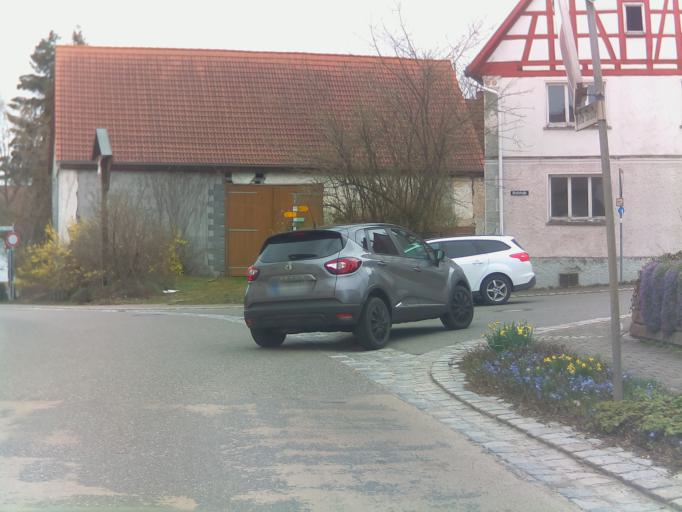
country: DE
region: Baden-Wuerttemberg
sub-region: Tuebingen Region
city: Schelklingen
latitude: 48.3875
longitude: 9.6640
